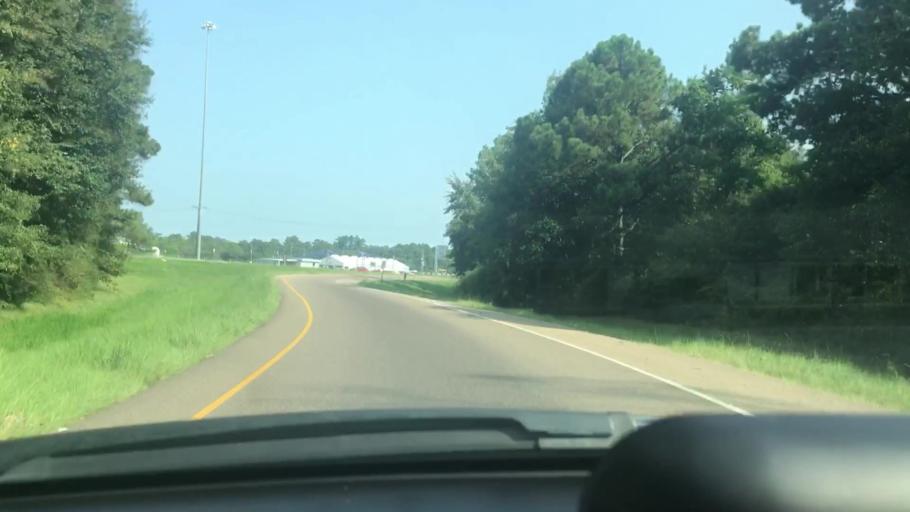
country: US
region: Louisiana
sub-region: Tangipahoa Parish
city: Hammond
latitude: 30.5023
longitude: -90.5049
